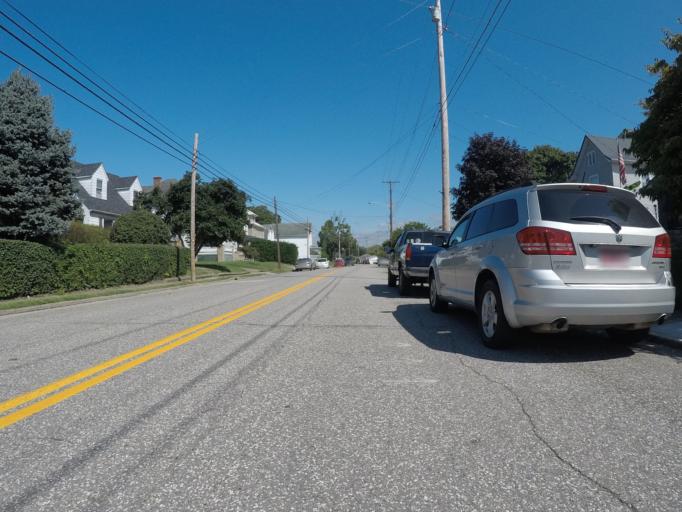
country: US
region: Kentucky
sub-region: Boyd County
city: Catlettsburg
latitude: 38.4081
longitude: -82.5987
